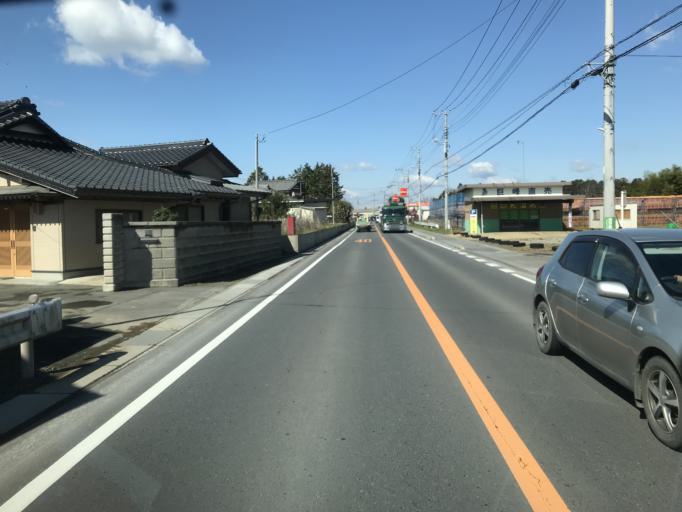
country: JP
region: Ibaraki
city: Ishioka
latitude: 36.0945
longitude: 140.3425
